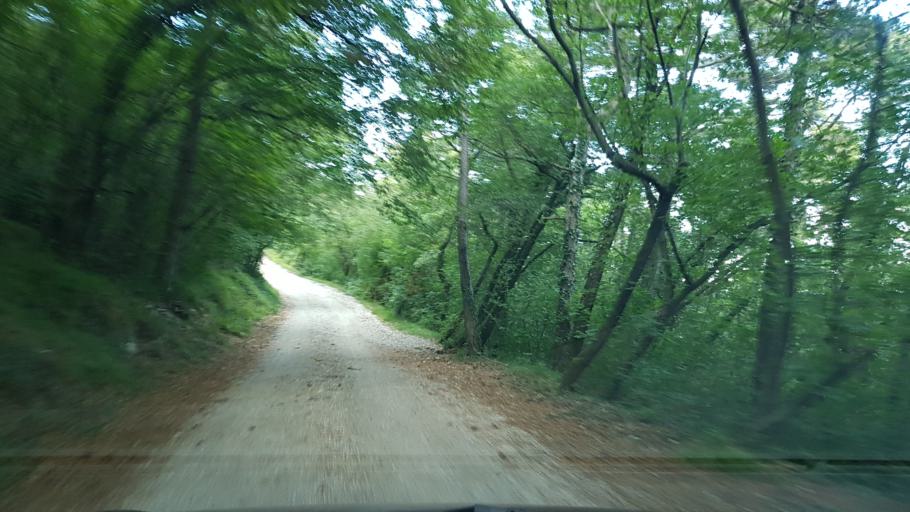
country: SI
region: Nova Gorica
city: Prvacina
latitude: 45.8553
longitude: 13.7028
